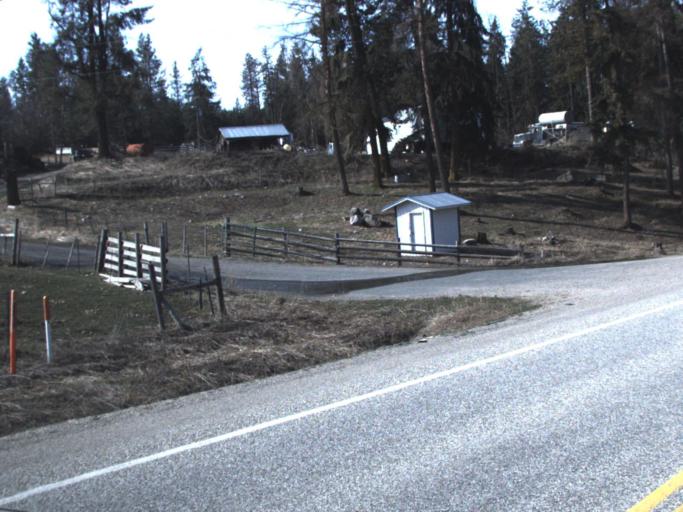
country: US
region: Washington
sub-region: Stevens County
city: Colville
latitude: 48.5146
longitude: -117.8003
